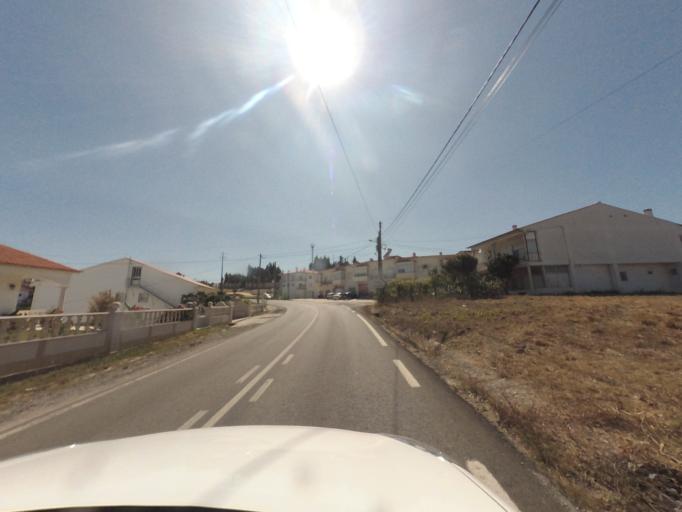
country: PT
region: Leiria
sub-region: Alcobaca
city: Turquel
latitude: 39.4826
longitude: -8.9865
